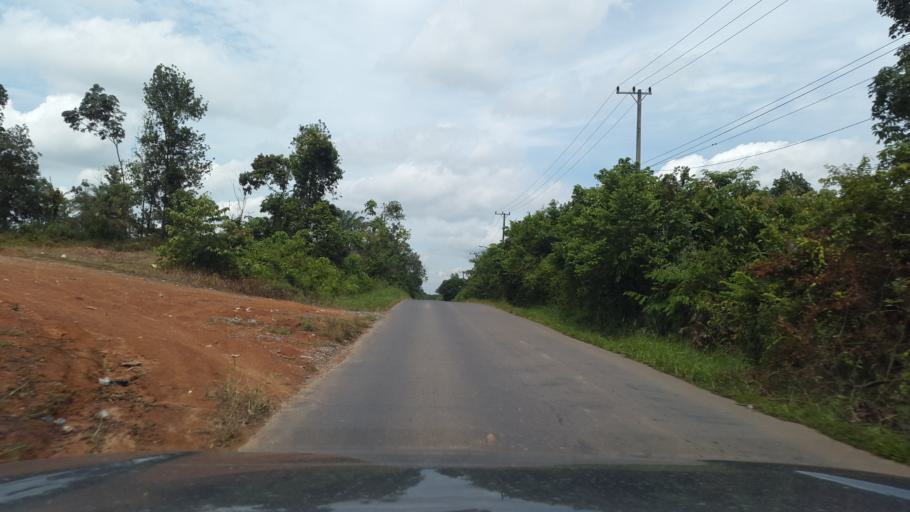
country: ID
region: South Sumatra
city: Gunungmegang Dalam
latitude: -3.3753
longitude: 103.9466
